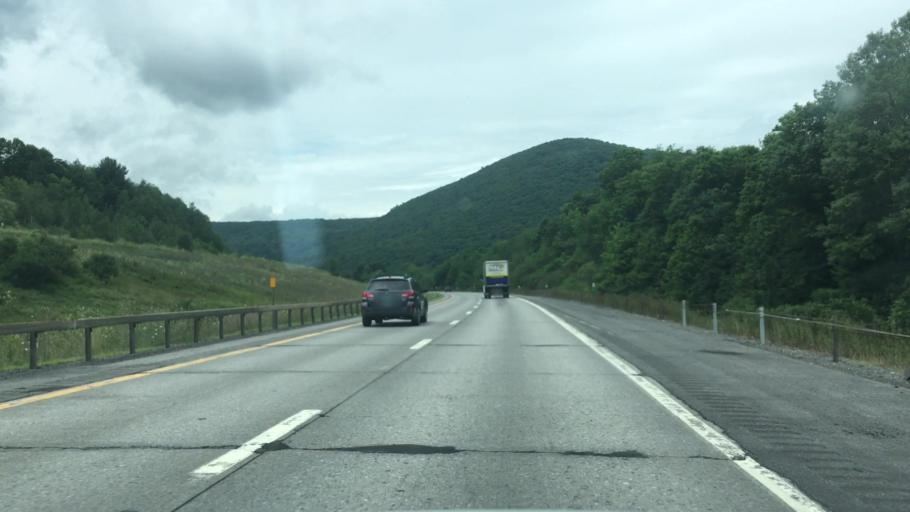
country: US
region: New York
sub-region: Otsego County
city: Worcester
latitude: 42.6499
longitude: -74.6242
